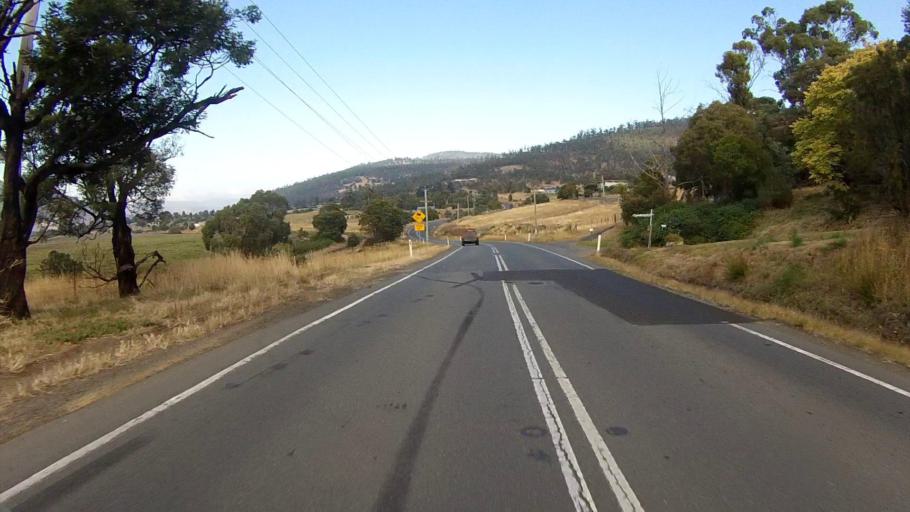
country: AU
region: Tasmania
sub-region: Brighton
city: Bridgewater
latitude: -42.7275
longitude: 147.1872
